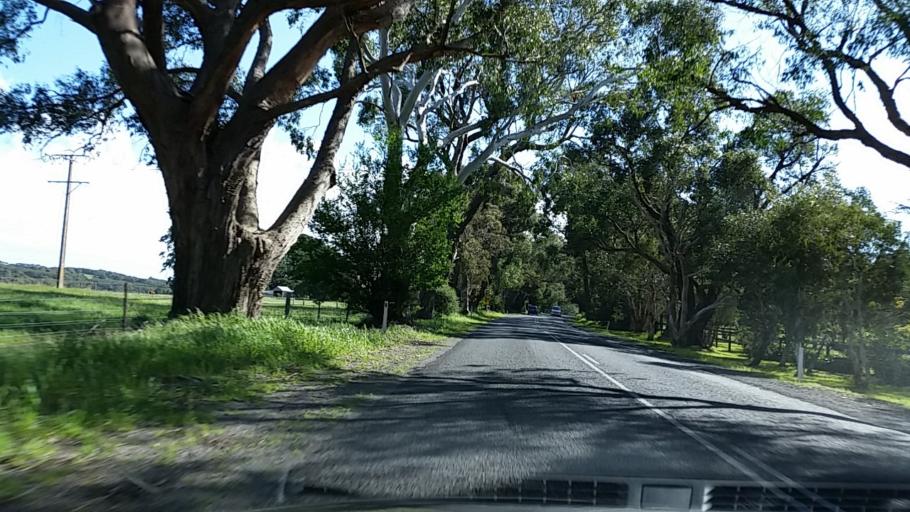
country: AU
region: South Australia
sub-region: Alexandrina
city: Mount Compass
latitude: -35.2657
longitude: 138.6451
